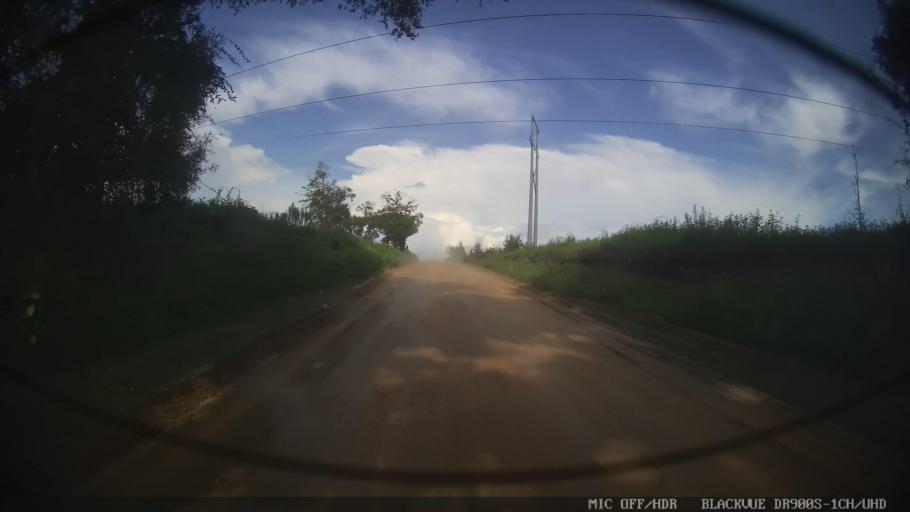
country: US
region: Georgia
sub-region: Lowndes County
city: Valdosta
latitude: 30.6180
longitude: -83.2319
